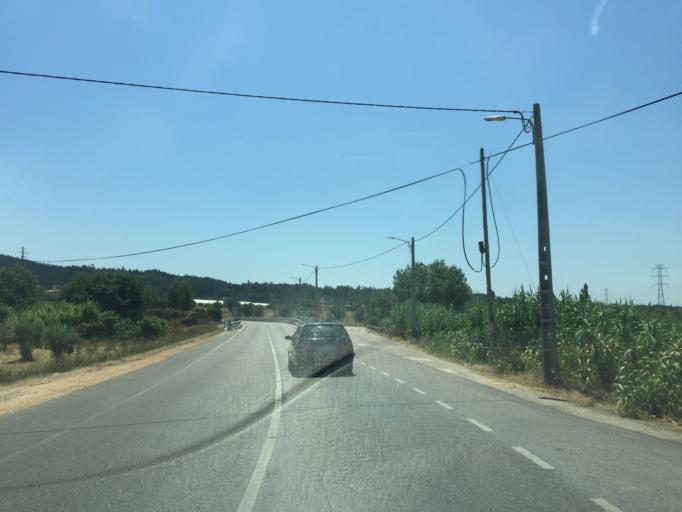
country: PT
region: Santarem
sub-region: Tomar
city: Tomar
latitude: 39.5926
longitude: -8.3608
